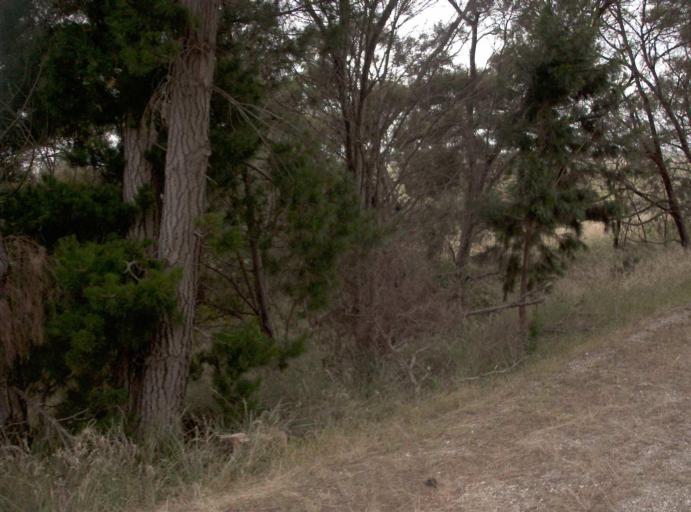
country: AU
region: Victoria
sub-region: Wellington
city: Sale
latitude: -38.1968
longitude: 147.3014
